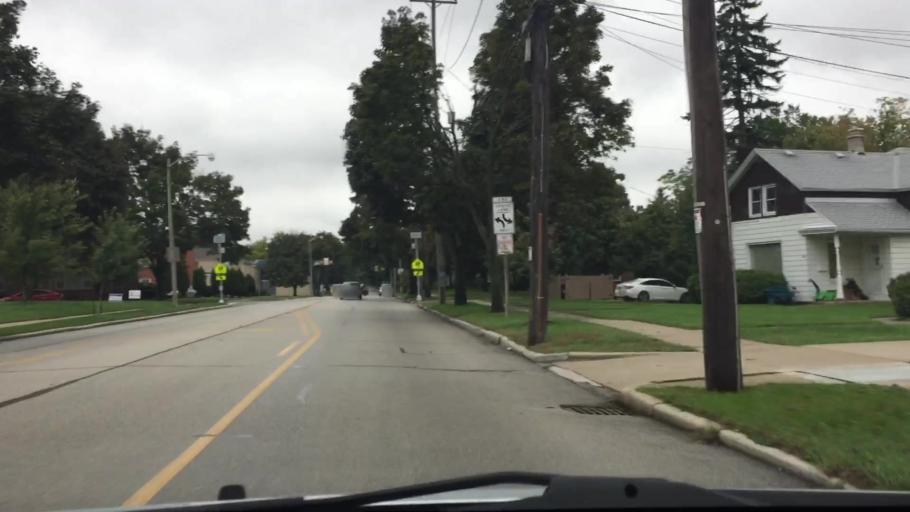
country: US
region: Wisconsin
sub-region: Milwaukee County
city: Wauwatosa
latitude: 43.0405
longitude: -88.0145
